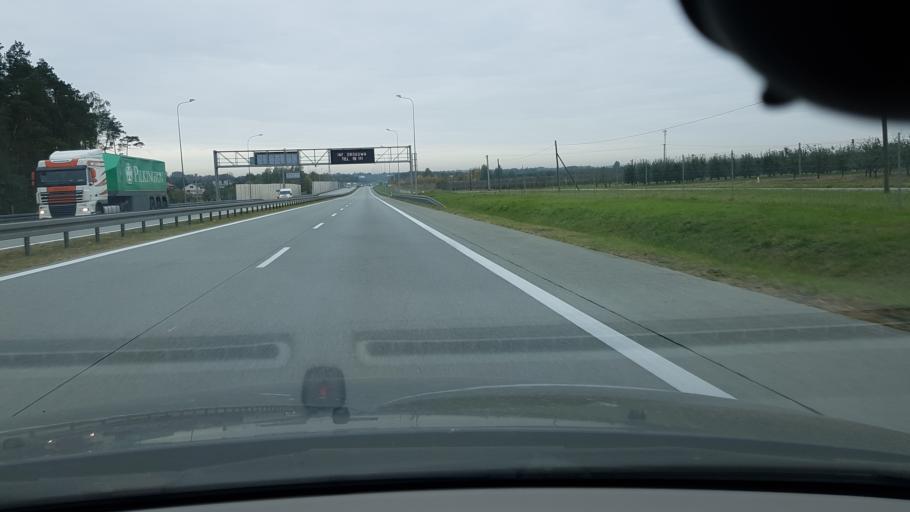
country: PL
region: Lodz Voivodeship
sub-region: Powiat skierniewicki
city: Kowiesy
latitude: 51.8968
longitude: 20.4283
